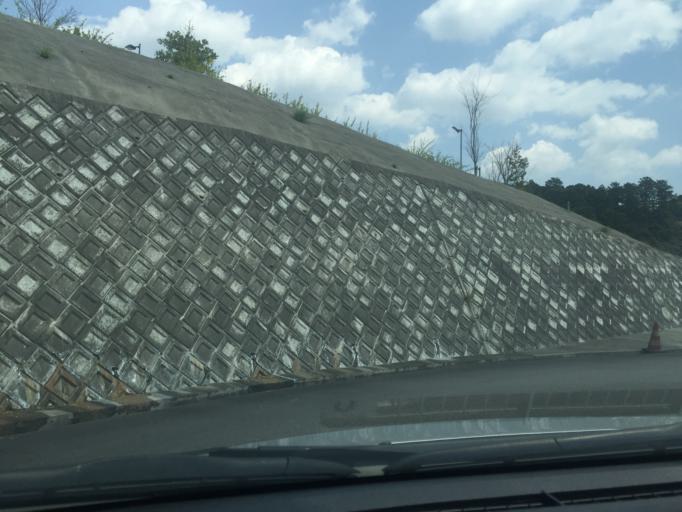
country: JP
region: Shizuoka
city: Kakegawa
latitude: 34.8381
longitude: 138.0343
